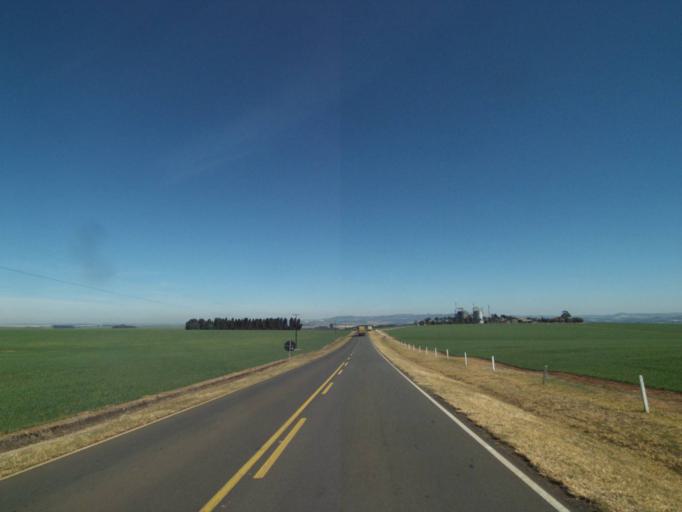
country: BR
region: Parana
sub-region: Tibagi
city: Tibagi
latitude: -24.5206
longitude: -50.3515
